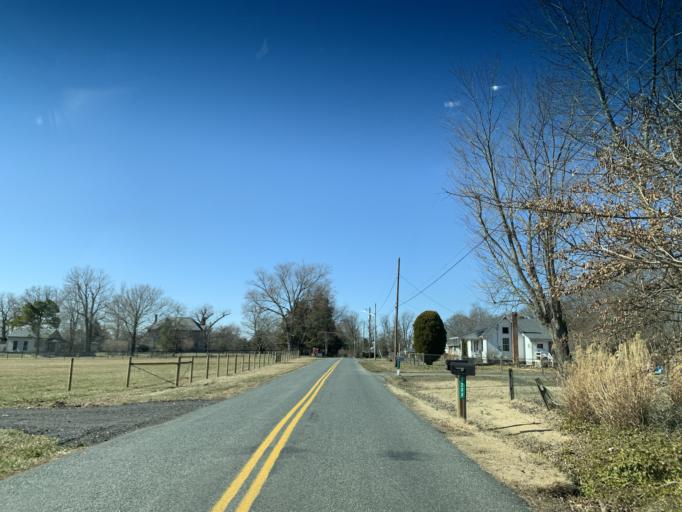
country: US
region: Maryland
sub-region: Harford County
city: Aberdeen
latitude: 39.6360
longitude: -76.1996
